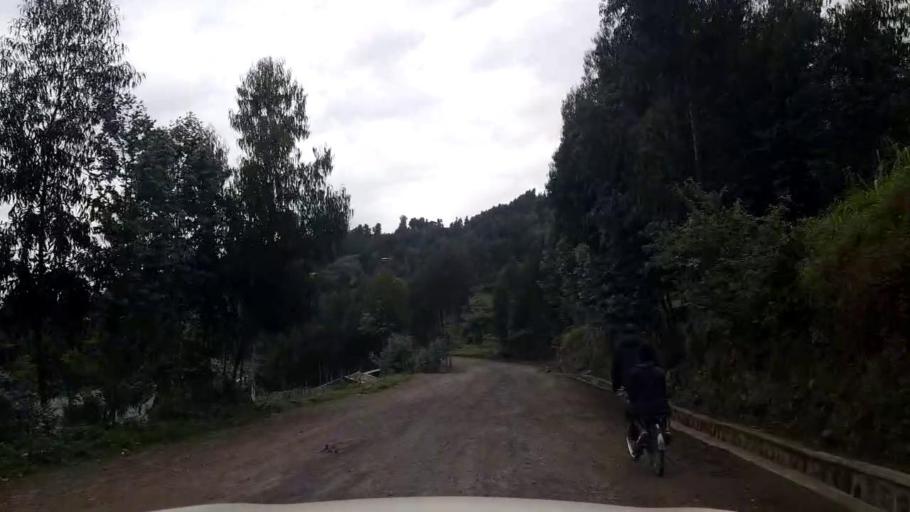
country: RW
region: Northern Province
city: Musanze
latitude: -1.5174
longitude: 29.5345
